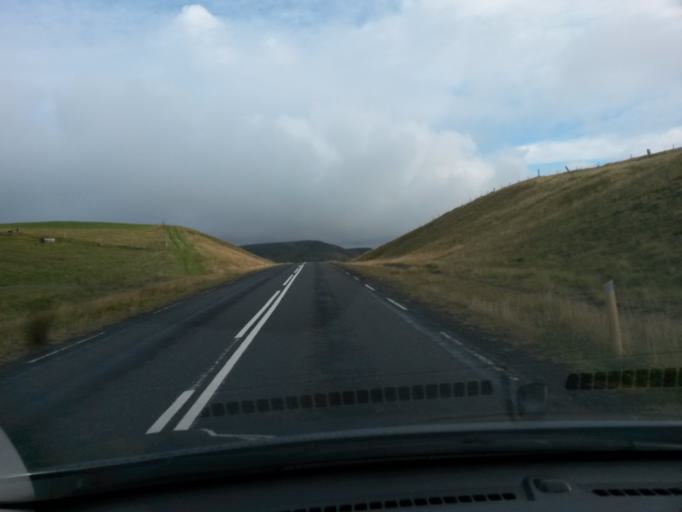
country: IS
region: South
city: Vestmannaeyjar
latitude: 63.4364
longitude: -19.1602
